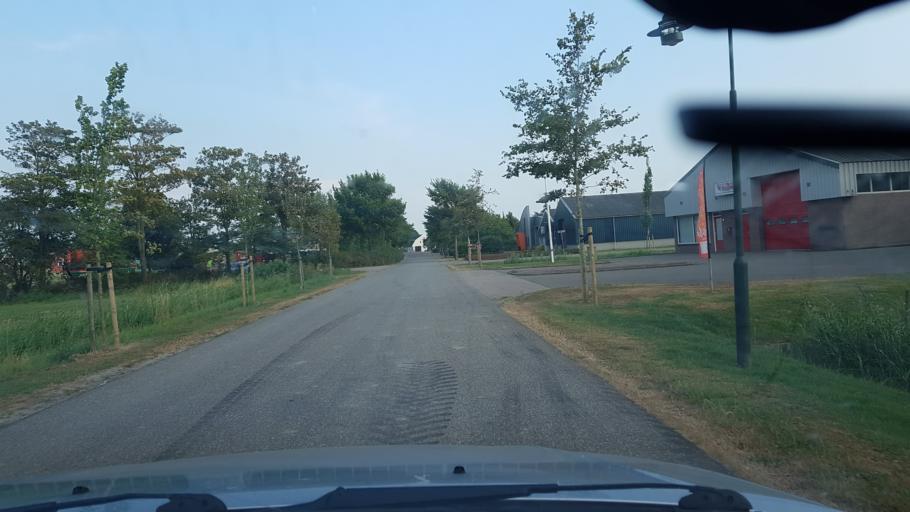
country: NL
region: Friesland
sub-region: Gemeente Ferwerderadiel
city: Burdaard
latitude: 53.2980
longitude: 5.8774
